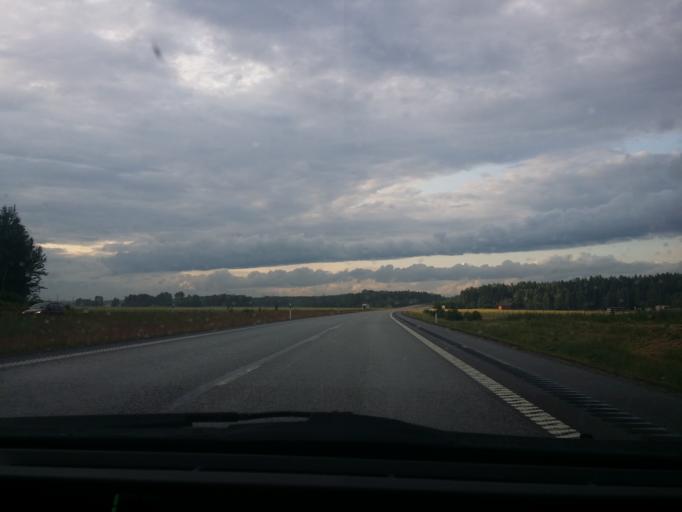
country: SE
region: Vaestmanland
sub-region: Arboga Kommun
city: Arboga
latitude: 59.4530
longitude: 15.8980
